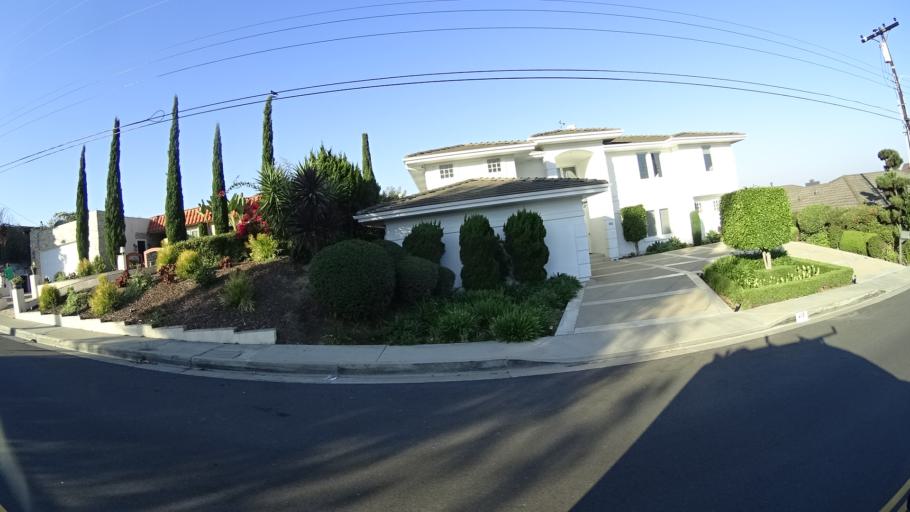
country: US
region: California
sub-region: Orange County
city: San Clemente
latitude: 33.4324
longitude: -117.6020
